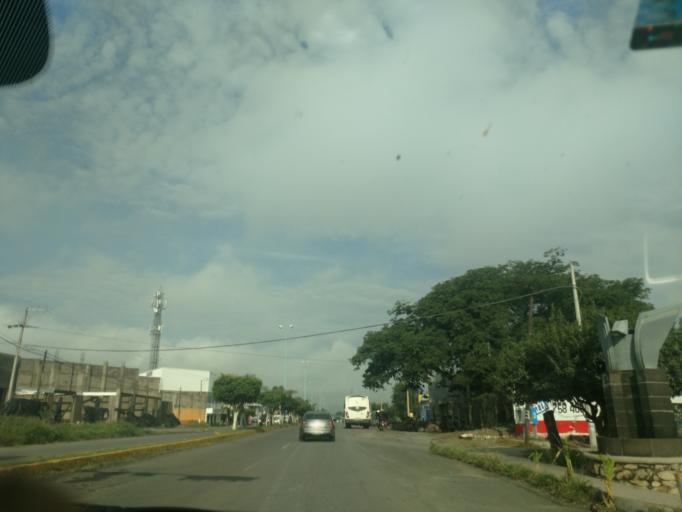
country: MX
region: Jalisco
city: Ameca
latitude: 20.5370
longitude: -104.0365
